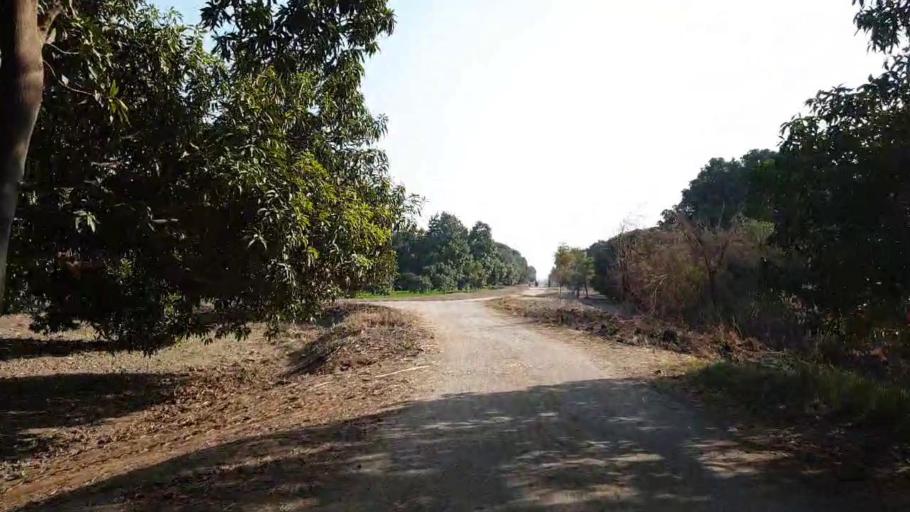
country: PK
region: Sindh
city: Tando Adam
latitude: 25.6028
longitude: 68.6155
